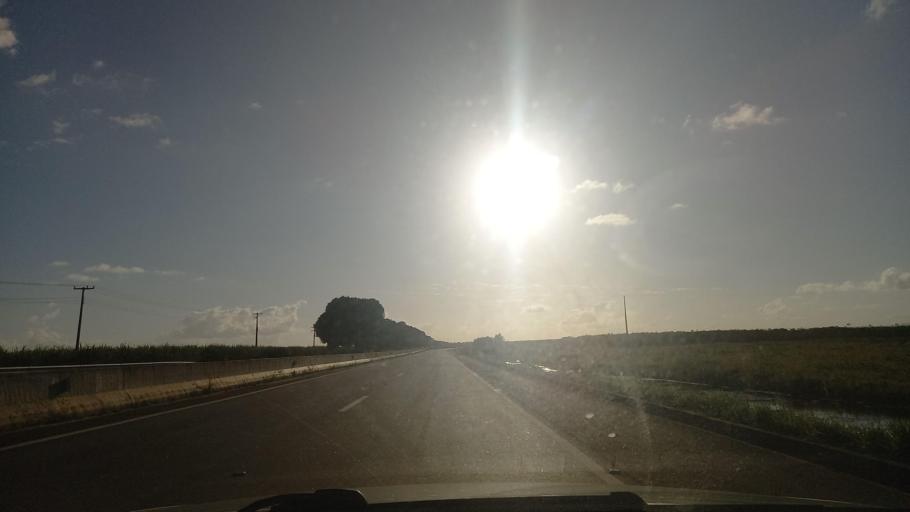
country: BR
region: Alagoas
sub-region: Campo Alegre
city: Campo Alegre
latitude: -9.8006
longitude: -36.2862
